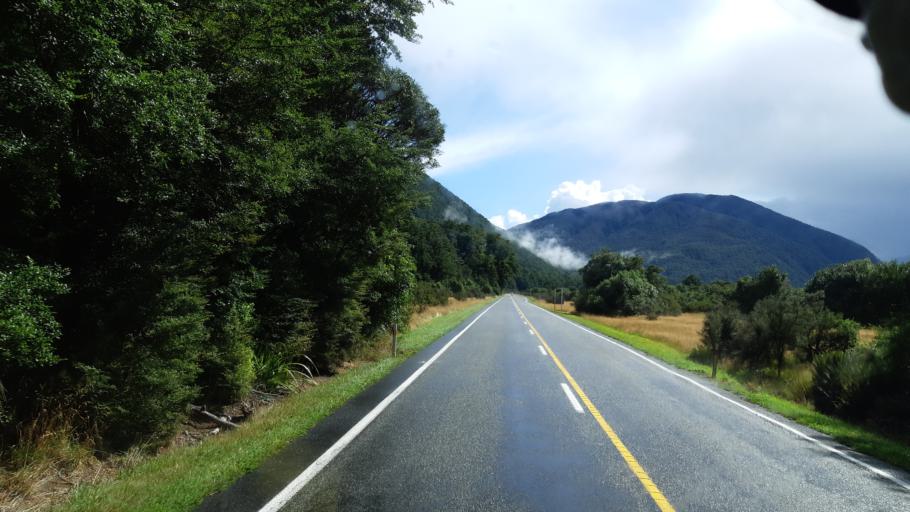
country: NZ
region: Canterbury
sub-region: Hurunui District
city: Amberley
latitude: -42.3821
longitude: 172.2961
